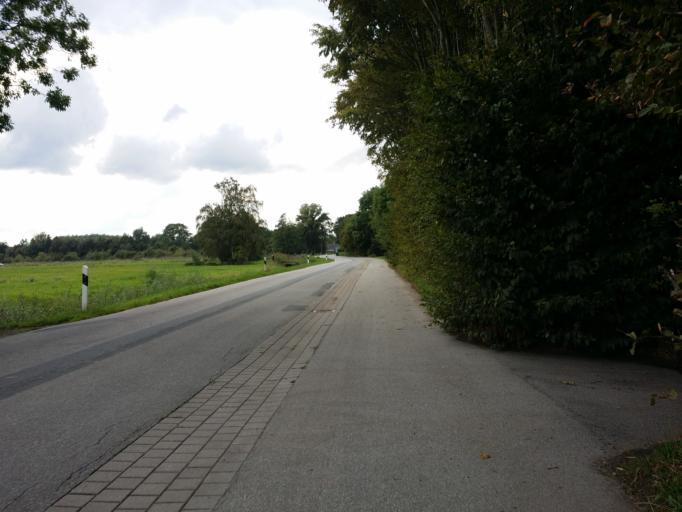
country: DE
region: Lower Saxony
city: Oederquart
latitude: 53.7819
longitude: 9.2510
